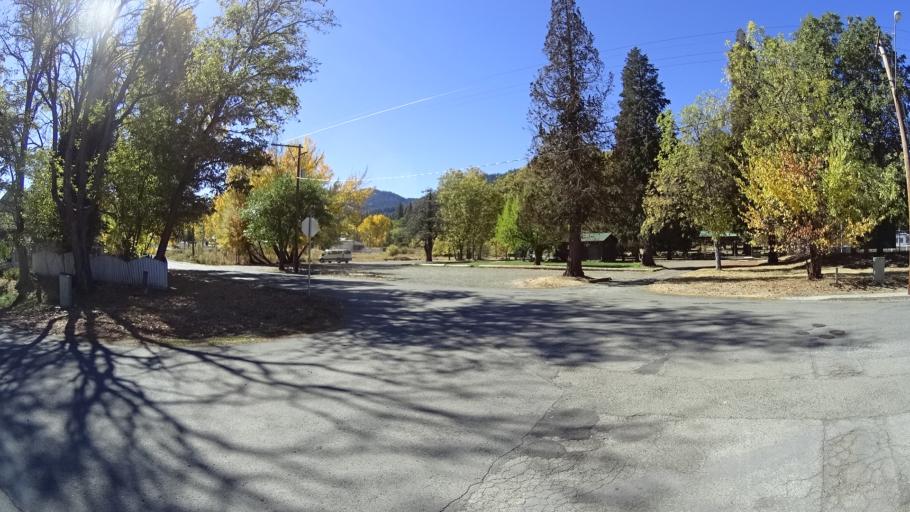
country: US
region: California
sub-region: Siskiyou County
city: Yreka
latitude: 41.4594
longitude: -122.8983
